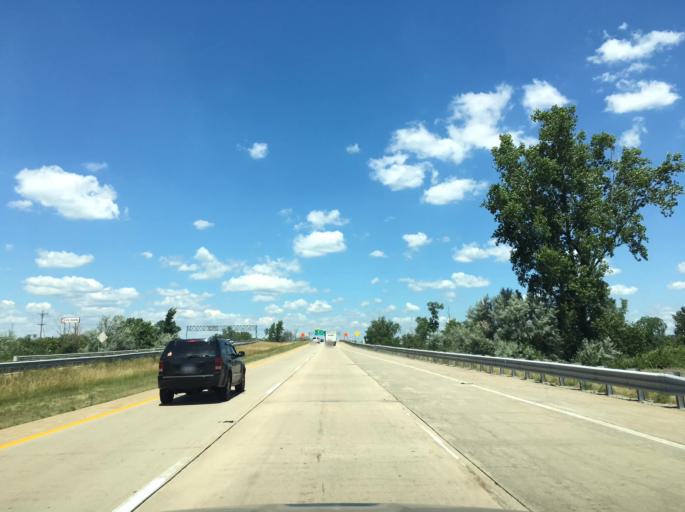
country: US
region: Michigan
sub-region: Midland County
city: Midland
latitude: 43.6058
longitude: -84.1615
